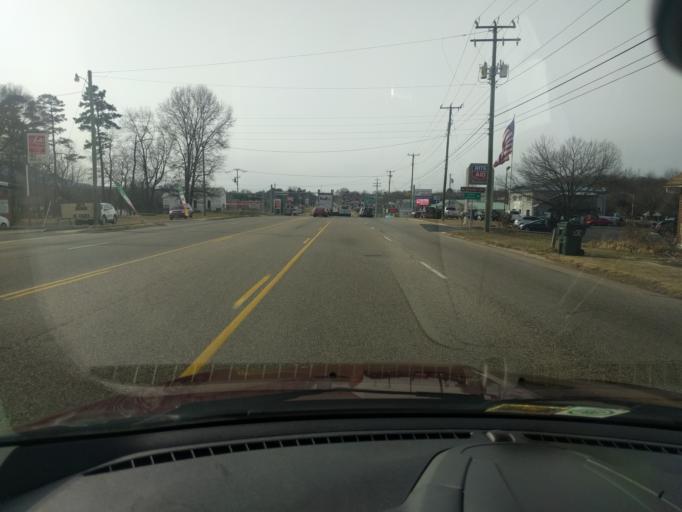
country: US
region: Virginia
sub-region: Augusta County
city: Stuarts Draft
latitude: 38.0352
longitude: -79.0334
